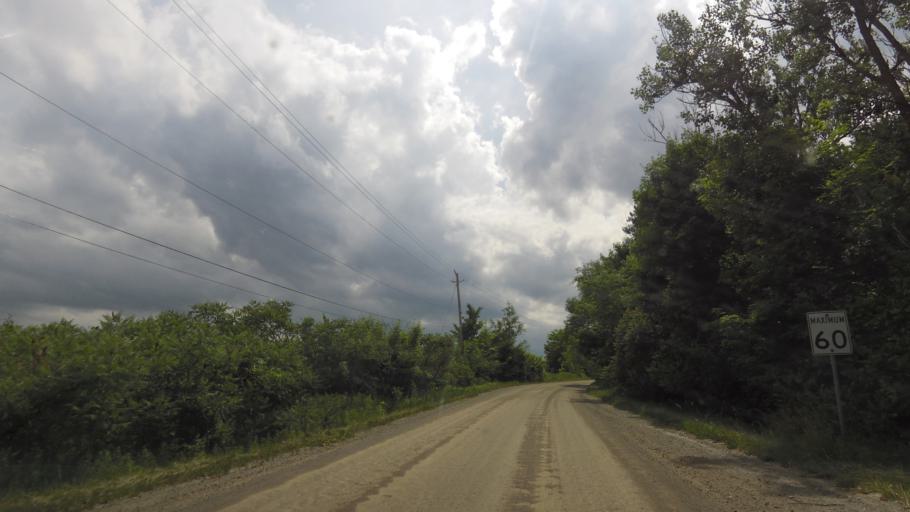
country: CA
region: Ontario
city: Orangeville
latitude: 43.8747
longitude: -79.9306
